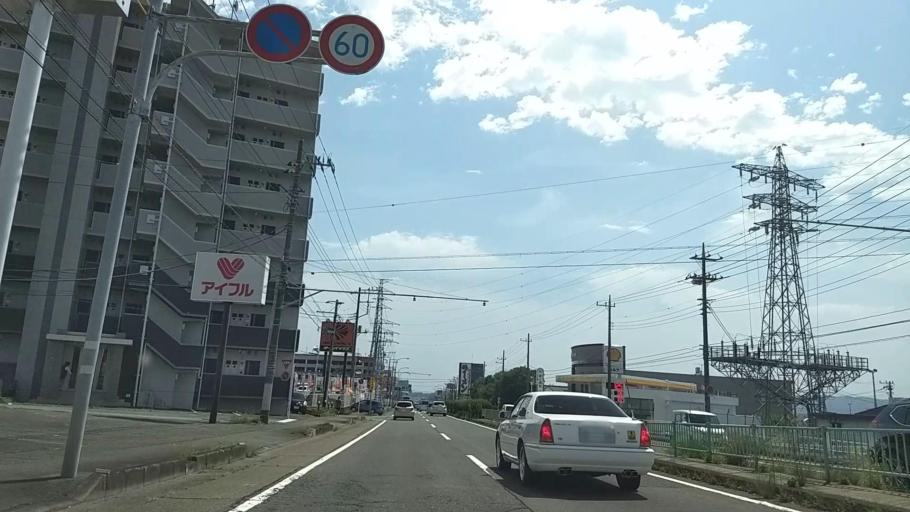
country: JP
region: Shizuoka
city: Fujinomiya
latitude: 35.2431
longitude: 138.6187
